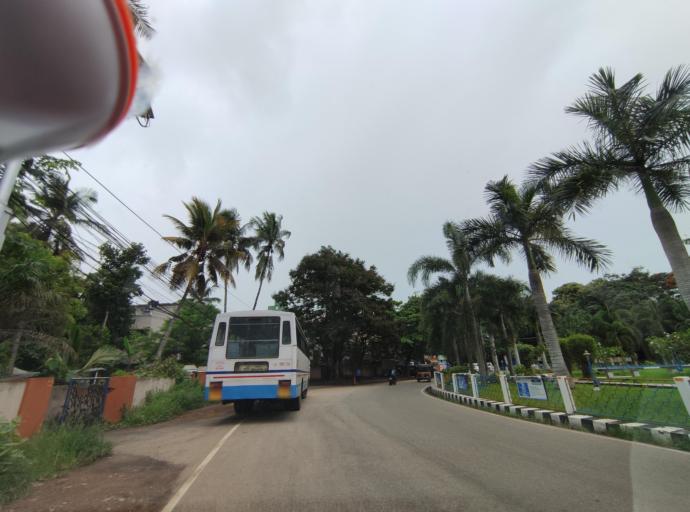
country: IN
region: Kerala
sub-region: Thiruvananthapuram
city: Thiruvananthapuram
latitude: 8.4908
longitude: 76.9735
